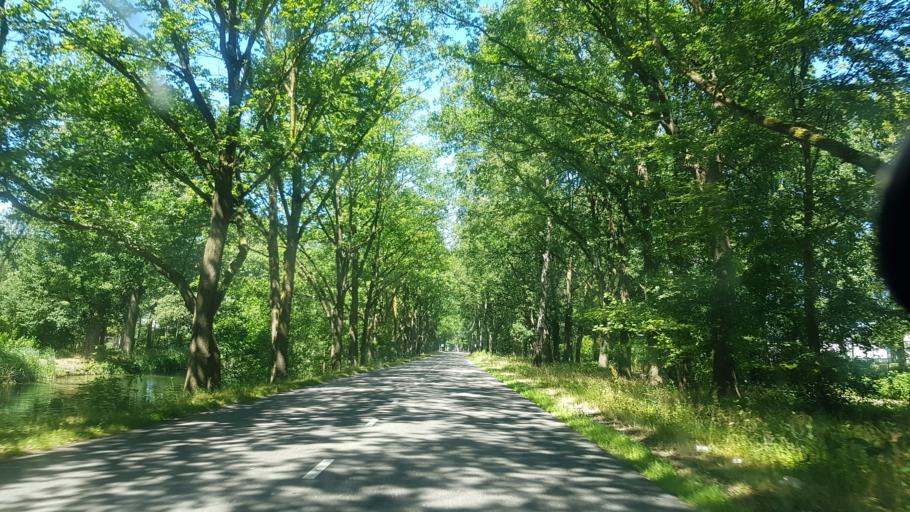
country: NL
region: Gelderland
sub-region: Gemeente Apeldoorn
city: Apeldoorn
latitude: 52.1830
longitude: 5.9900
